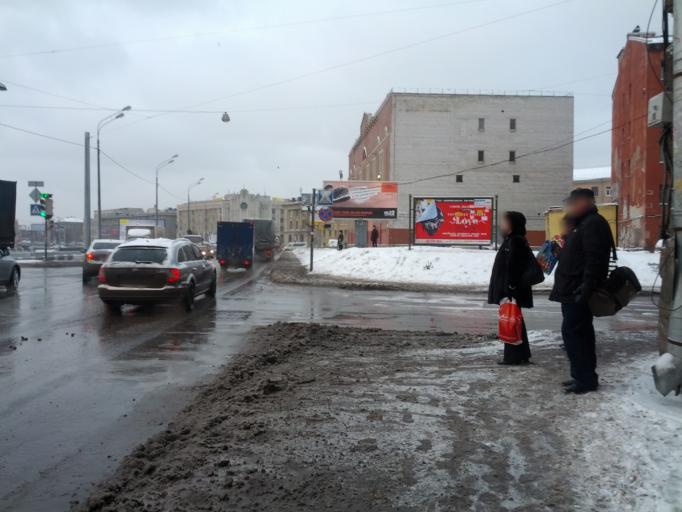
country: RU
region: St.-Petersburg
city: Centralniy
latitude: 59.9167
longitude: 30.3460
